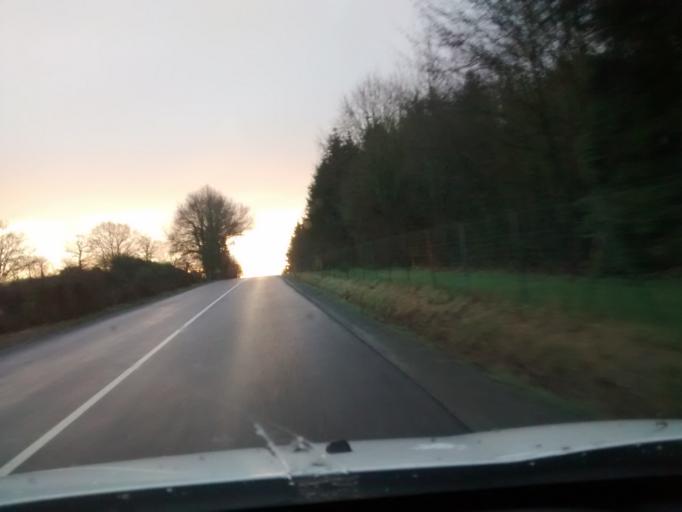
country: FR
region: Brittany
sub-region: Departement d'Ille-et-Vilaine
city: Louvigne-de-Bais
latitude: 48.0267
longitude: -1.3130
